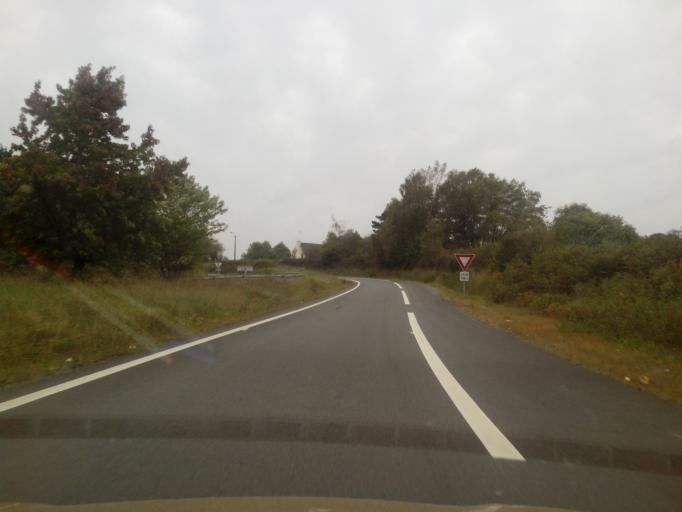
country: FR
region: Brittany
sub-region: Departement du Morbihan
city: Hennebont
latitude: 47.7982
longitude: -3.2405
